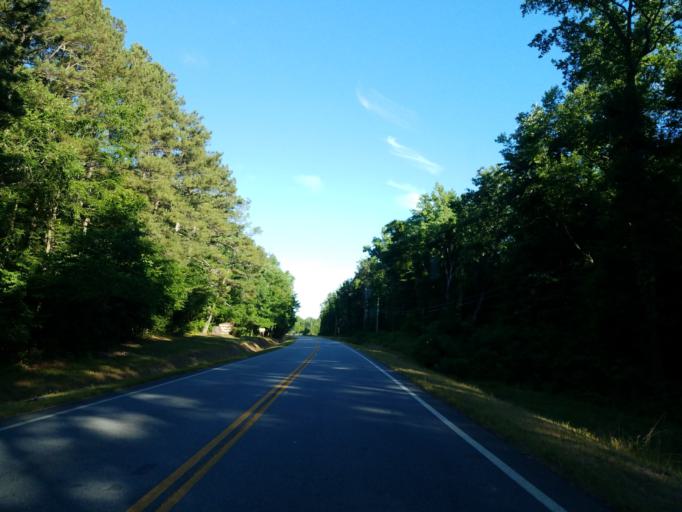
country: US
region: Georgia
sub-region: Gordon County
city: Calhoun
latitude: 34.6119
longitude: -85.0491
